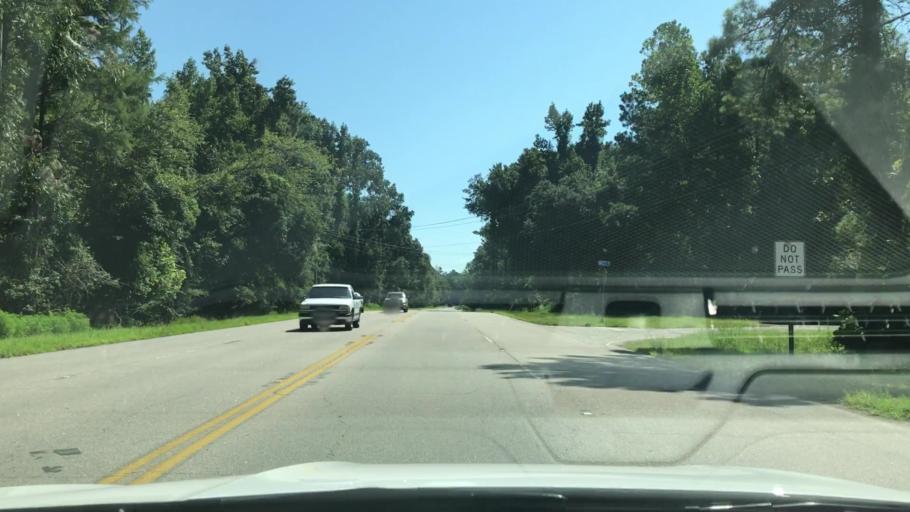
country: US
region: South Carolina
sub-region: Horry County
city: Conway
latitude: 33.8381
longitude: -79.0405
